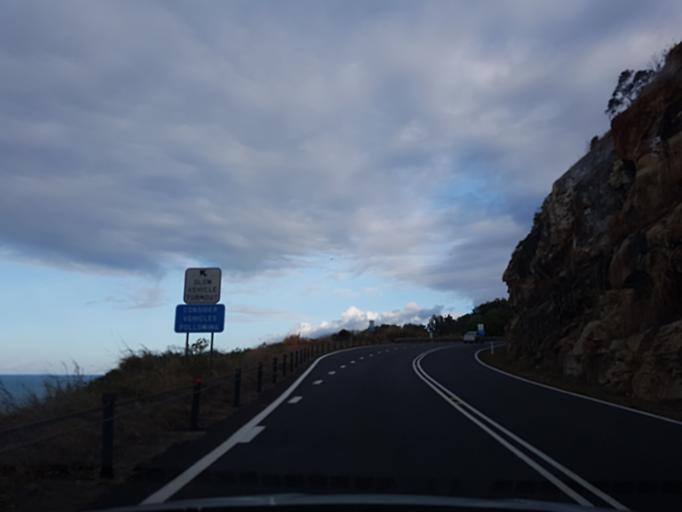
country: AU
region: Queensland
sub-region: Cairns
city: Palm Cove
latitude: -16.6431
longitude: 145.5644
